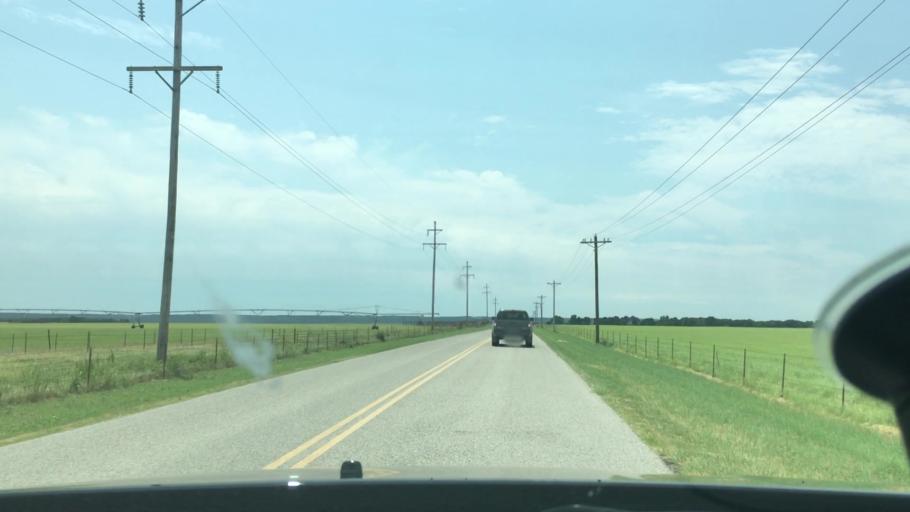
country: US
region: Oklahoma
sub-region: Love County
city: Marietta
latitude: 33.9202
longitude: -97.3521
